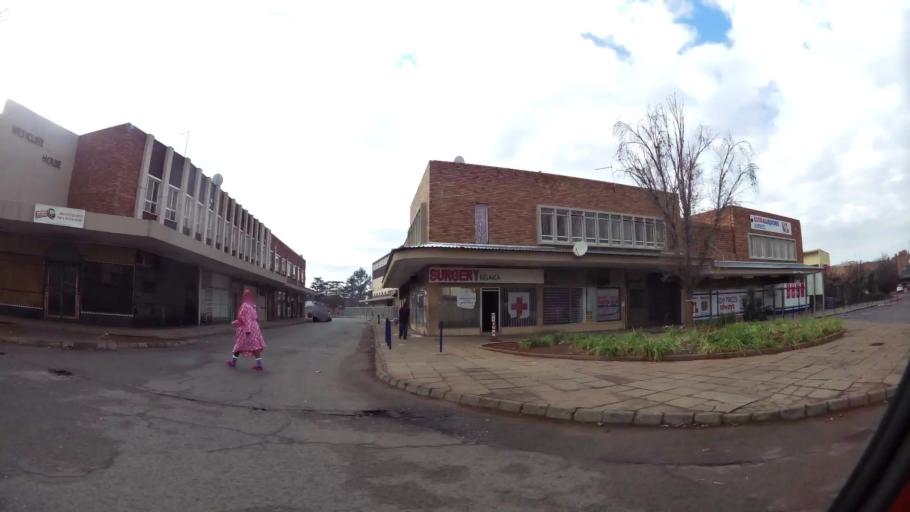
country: ZA
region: Gauteng
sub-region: Sedibeng District Municipality
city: Vanderbijlpark
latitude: -26.6948
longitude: 27.8252
